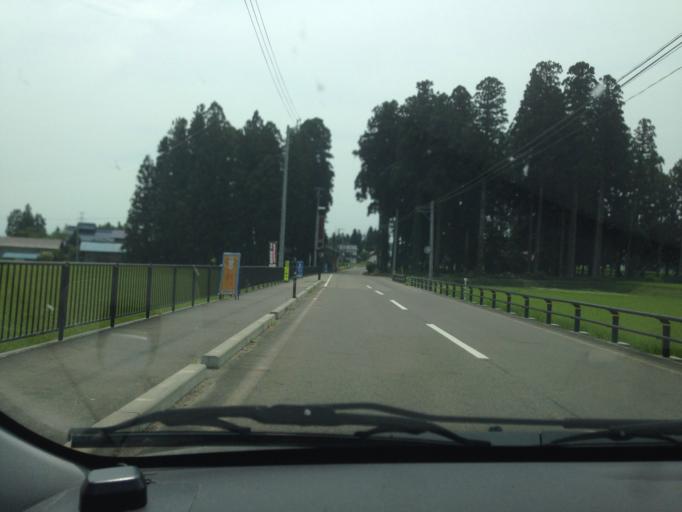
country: JP
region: Fukushima
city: Kitakata
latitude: 37.7042
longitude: 139.8461
